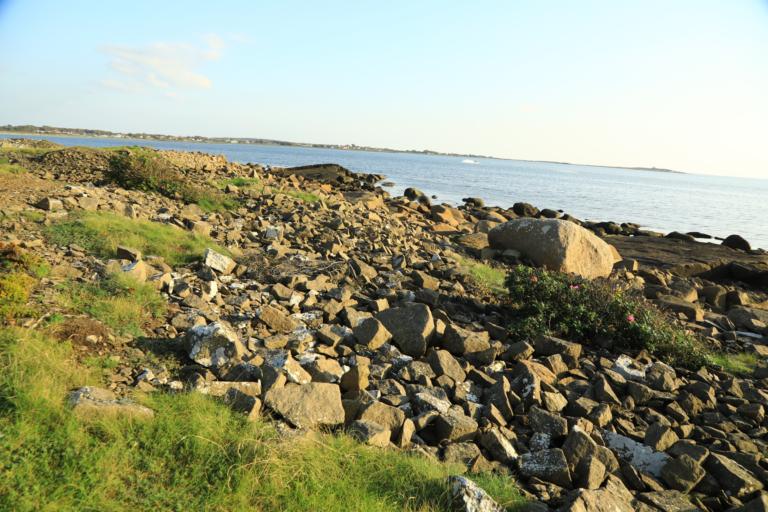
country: SE
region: Halland
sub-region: Varbergs Kommun
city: Varberg
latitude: 57.0833
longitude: 12.2436
